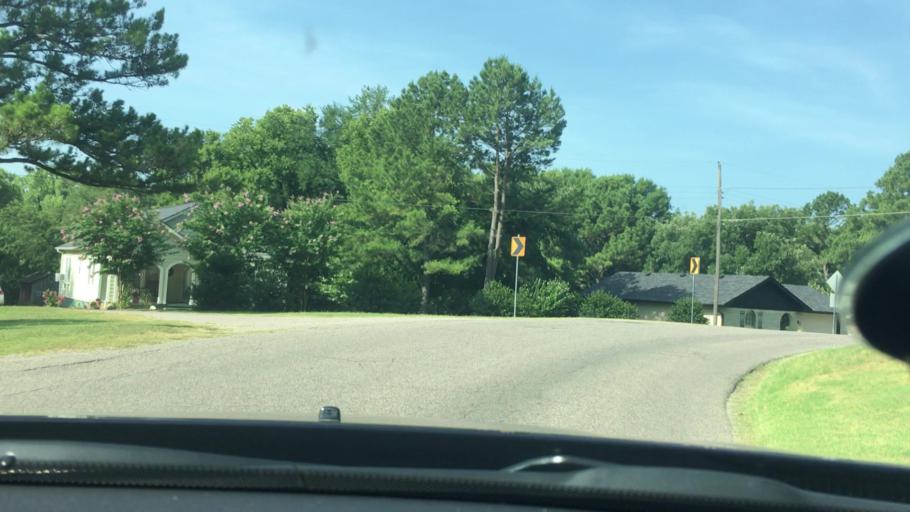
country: US
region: Oklahoma
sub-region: Pontotoc County
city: Ada
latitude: 34.7569
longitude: -96.6563
